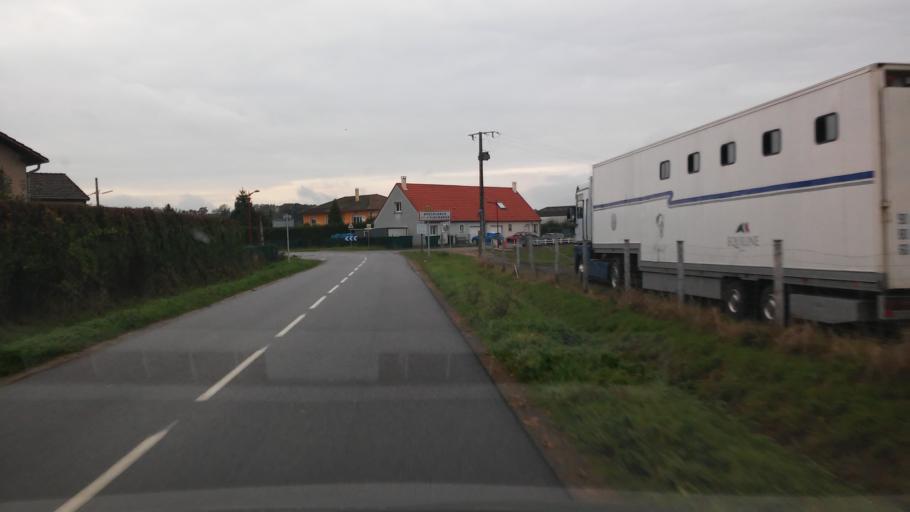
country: FR
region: Lorraine
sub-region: Departement de la Moselle
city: Boulay-Moselle
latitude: 49.1881
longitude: 6.4651
